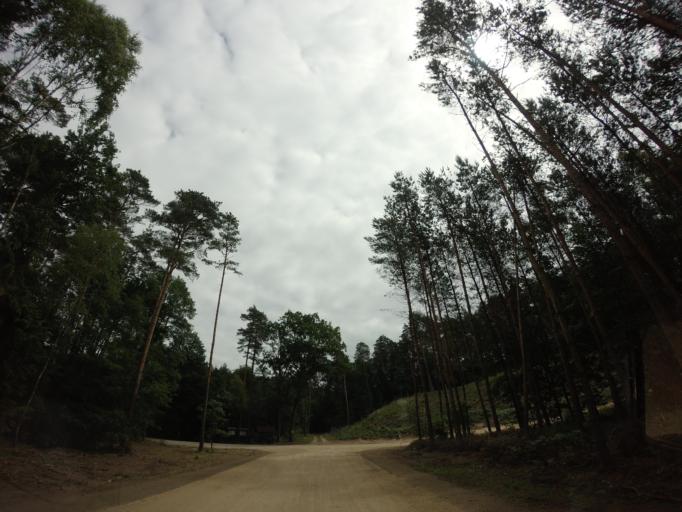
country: PL
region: Lubusz
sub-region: Powiat strzelecko-drezdenecki
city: Stare Kurowo
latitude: 52.8853
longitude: 15.6396
